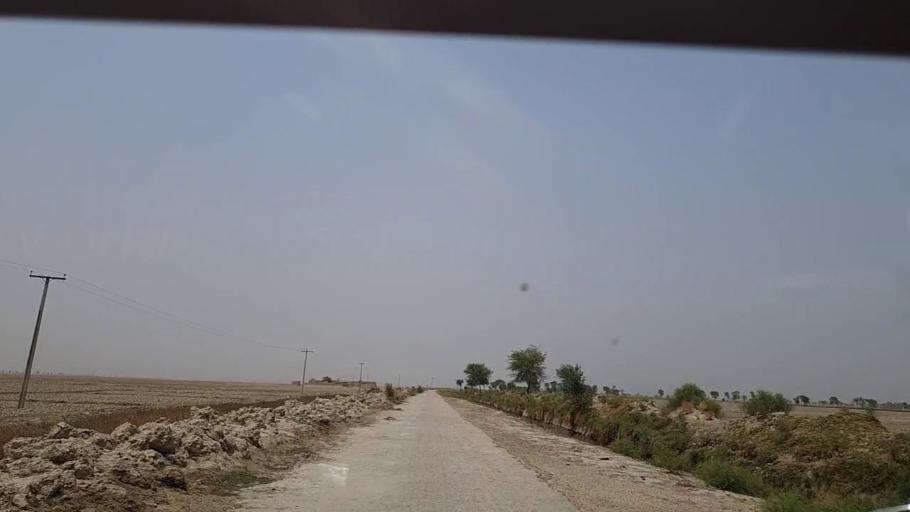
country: PK
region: Sindh
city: Khairpur Nathan Shah
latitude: 27.0363
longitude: 67.6191
